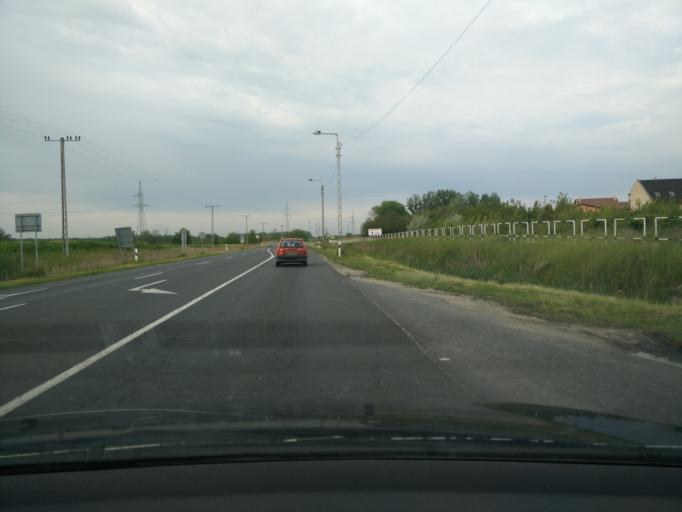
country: HU
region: Gyor-Moson-Sopron
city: Gyor
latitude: 47.6388
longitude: 17.6040
